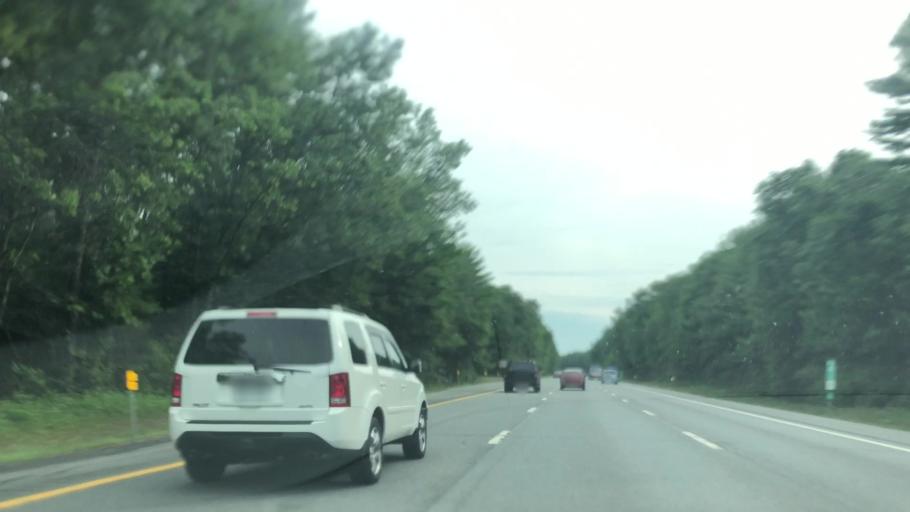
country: US
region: New York
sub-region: Warren County
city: West Glens Falls
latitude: 43.2507
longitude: -73.6851
